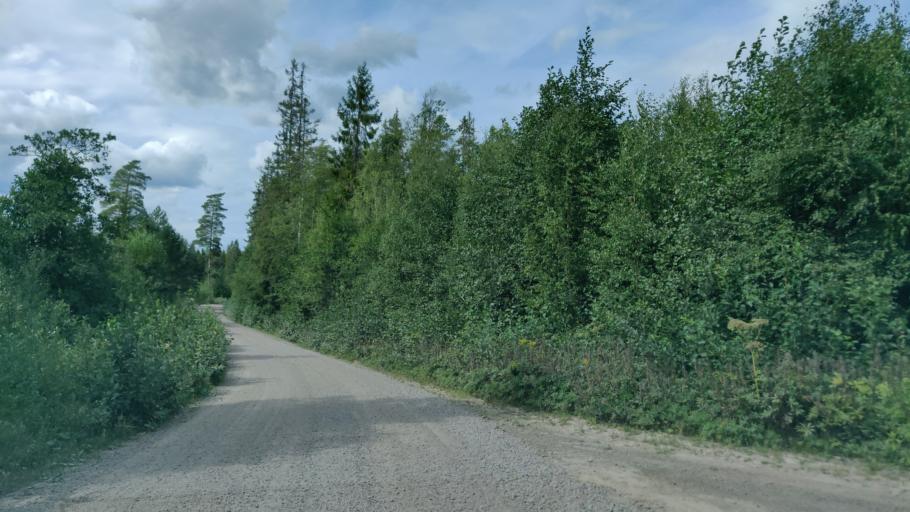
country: SE
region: Vaermland
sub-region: Hagfors Kommun
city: Hagfors
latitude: 60.0095
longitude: 13.7094
